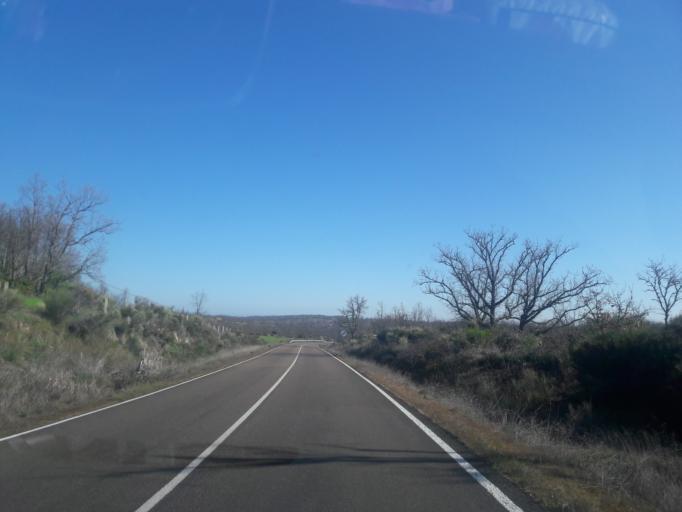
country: ES
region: Castille and Leon
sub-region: Provincia de Salamanca
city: Villasbuenas
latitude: 41.0846
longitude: -6.5598
